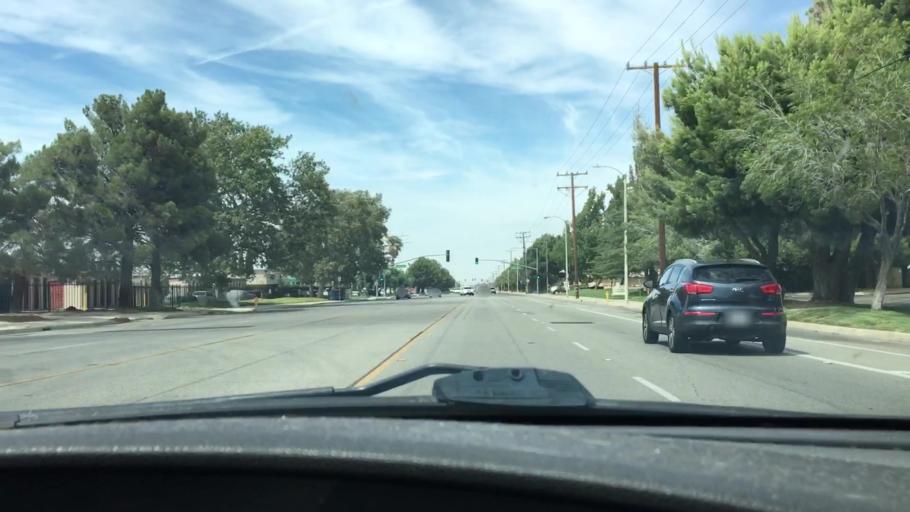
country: US
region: California
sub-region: Los Angeles County
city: Lancaster
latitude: 34.6699
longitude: -118.1301
